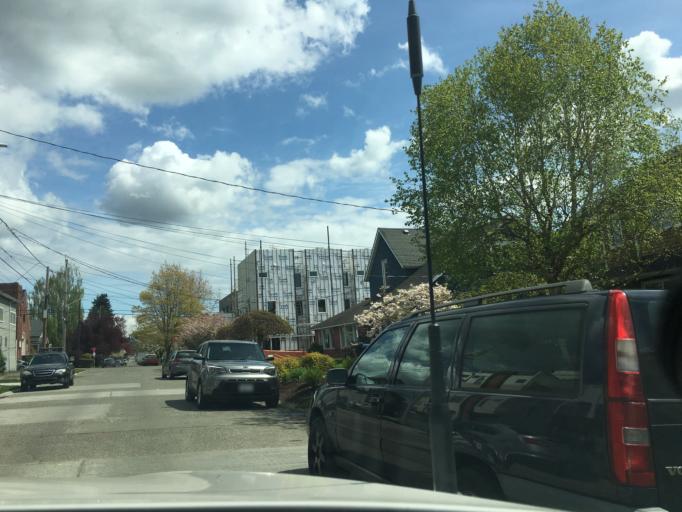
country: US
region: Washington
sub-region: King County
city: Seattle
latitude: 47.6731
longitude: -122.3858
